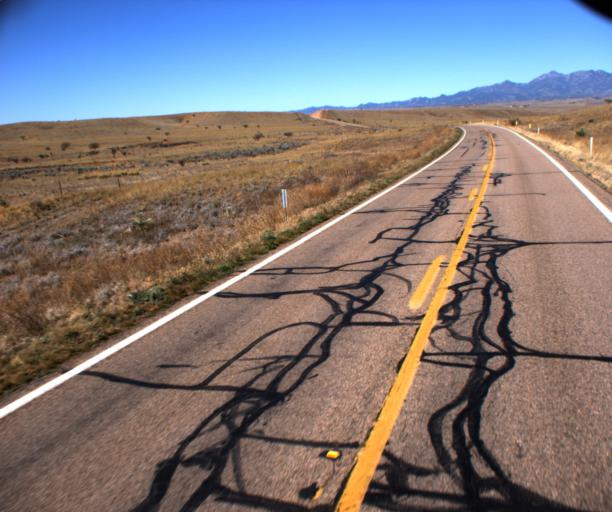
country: US
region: Arizona
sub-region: Cochise County
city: Huachuca City
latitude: 31.7103
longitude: -110.5716
